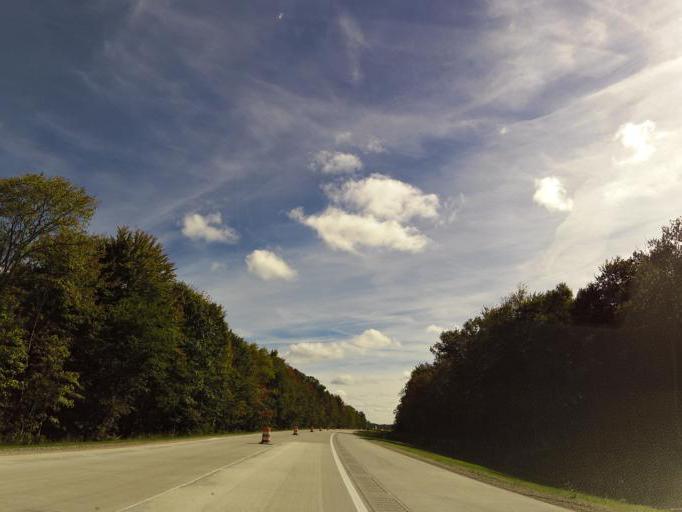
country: US
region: Michigan
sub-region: Macomb County
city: Memphis
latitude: 42.9745
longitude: -82.6591
